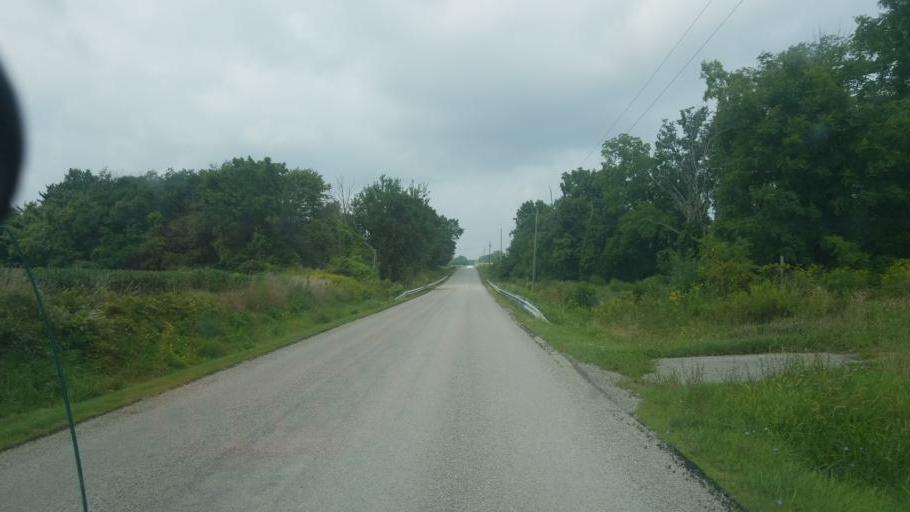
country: US
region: Ohio
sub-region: Huron County
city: Greenwich
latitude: 41.0540
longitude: -82.5219
